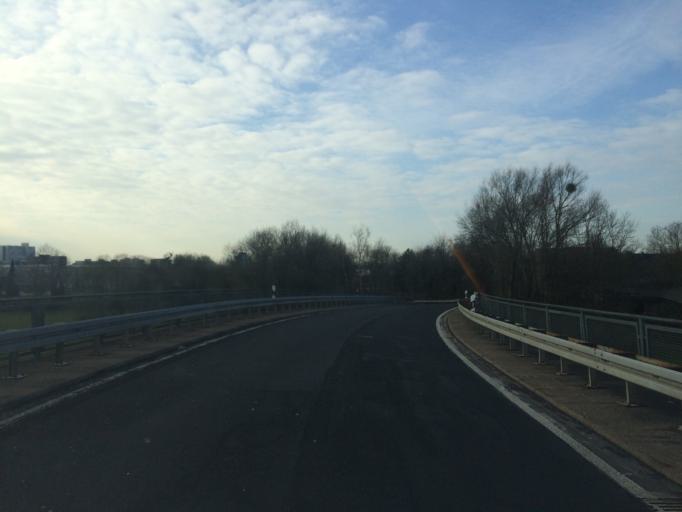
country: DE
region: North Rhine-Westphalia
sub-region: Regierungsbezirk Koln
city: Merheim
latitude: 50.9465
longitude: 7.0579
